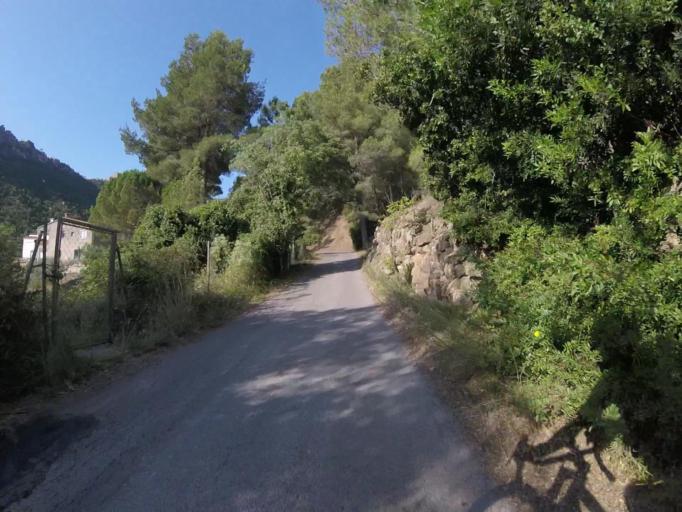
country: ES
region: Valencia
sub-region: Provincia de Castello
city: Benicassim
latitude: 40.0837
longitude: 0.0531
